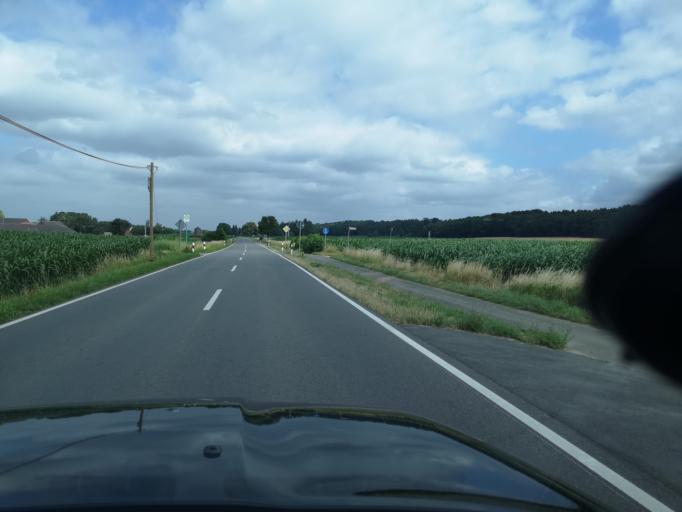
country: DE
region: North Rhine-Westphalia
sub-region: Regierungsbezirk Dusseldorf
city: Hamminkeln
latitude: 51.7347
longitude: 6.6501
